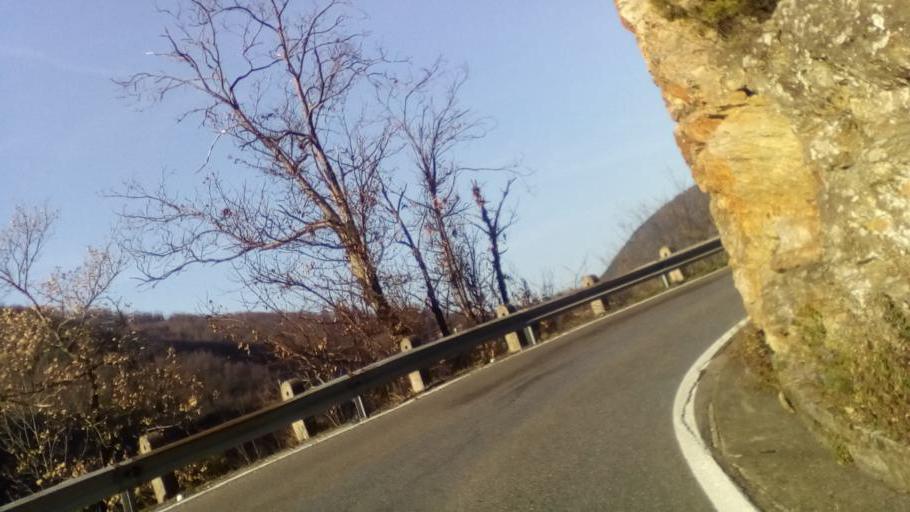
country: IT
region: Tuscany
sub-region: Provincia di Massa-Carrara
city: Montignoso
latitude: 44.0539
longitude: 10.1881
